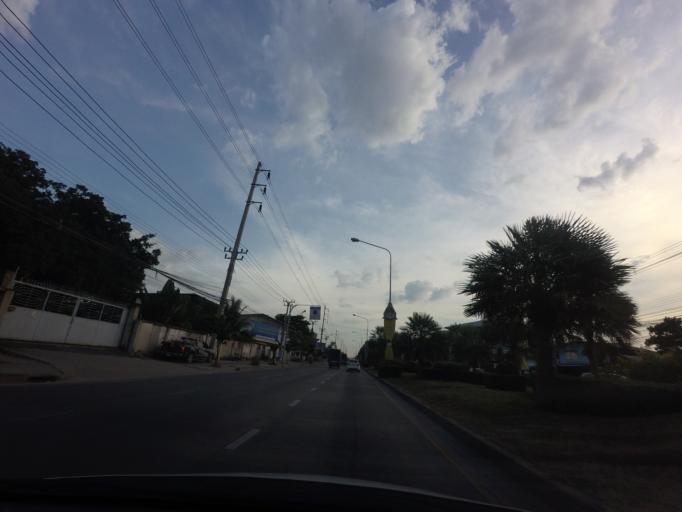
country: TH
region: Bangkok
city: Bang Khun Thian
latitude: 13.6396
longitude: 100.4325
